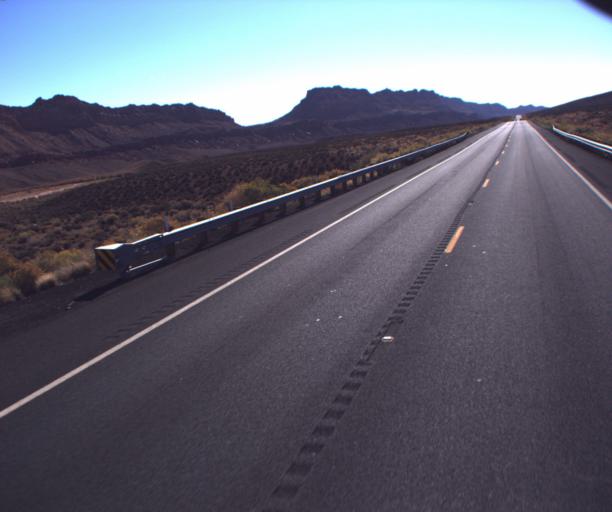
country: US
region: Arizona
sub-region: Coconino County
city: Tuba City
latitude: 36.2763
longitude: -111.4384
